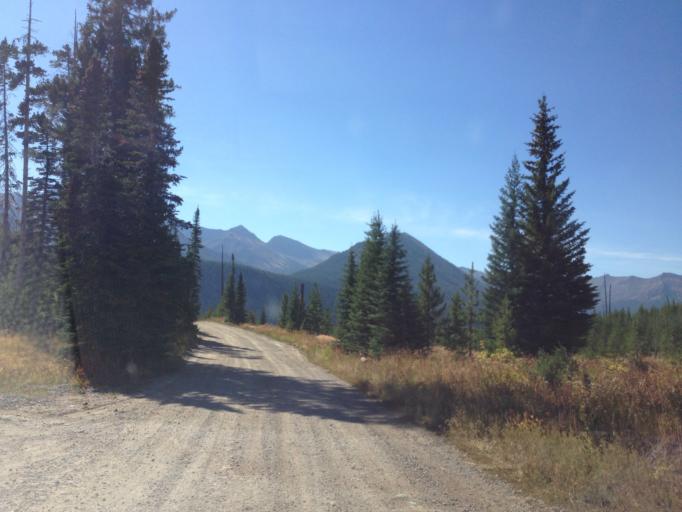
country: US
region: Montana
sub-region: Stillwater County
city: Absarokee
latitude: 45.0341
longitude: -109.9118
